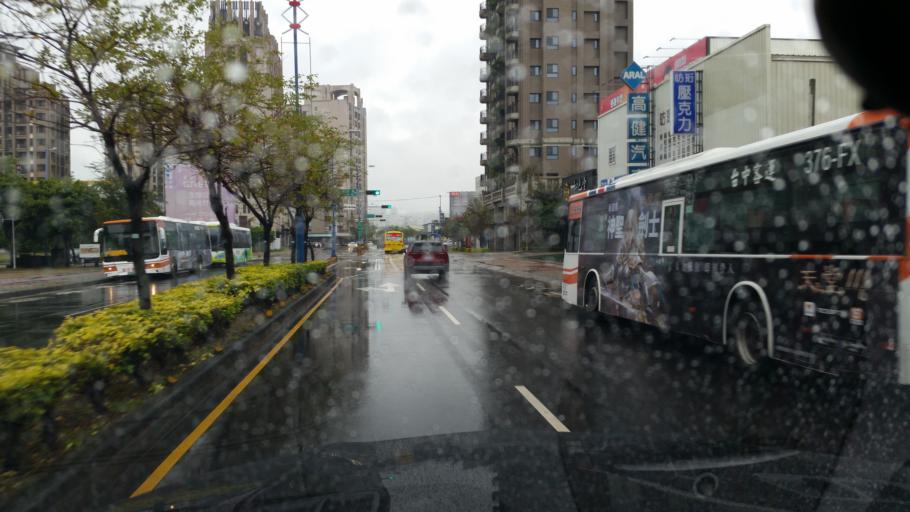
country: TW
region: Taiwan
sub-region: Taichung City
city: Taichung
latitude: 24.1852
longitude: 120.6421
